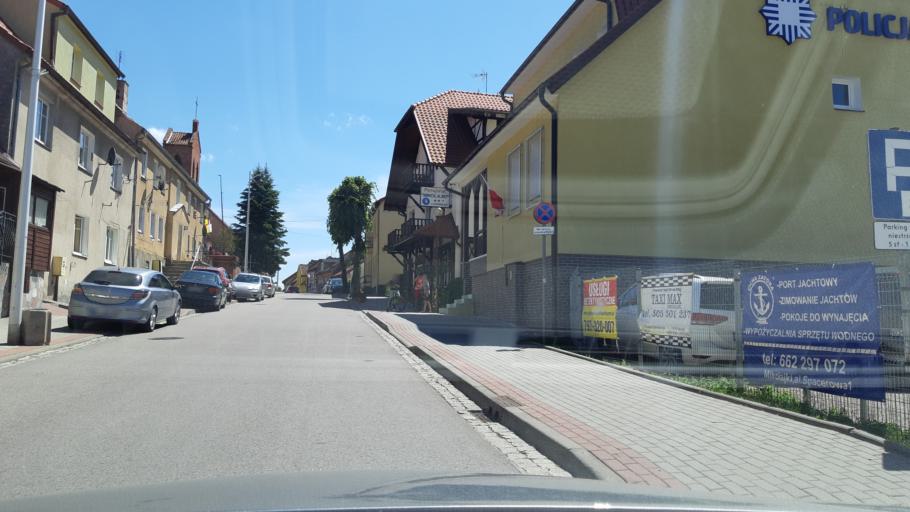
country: PL
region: Warmian-Masurian Voivodeship
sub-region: Powiat mragowski
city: Mikolajki
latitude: 53.7992
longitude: 21.5750
